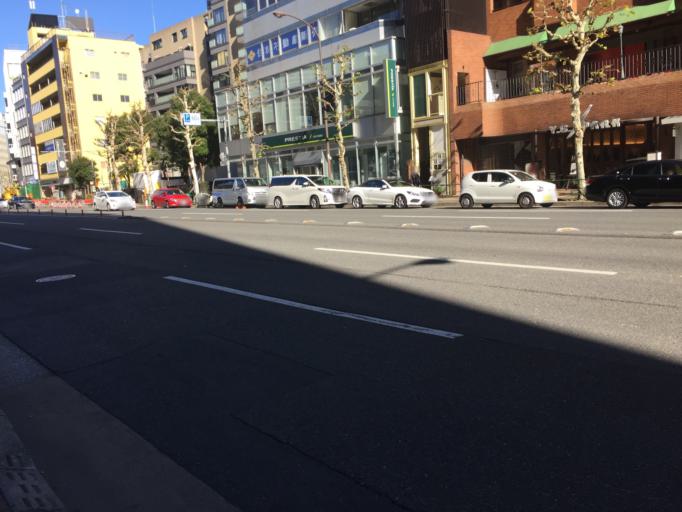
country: JP
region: Tokyo
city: Tokyo
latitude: 35.6516
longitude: 139.7222
